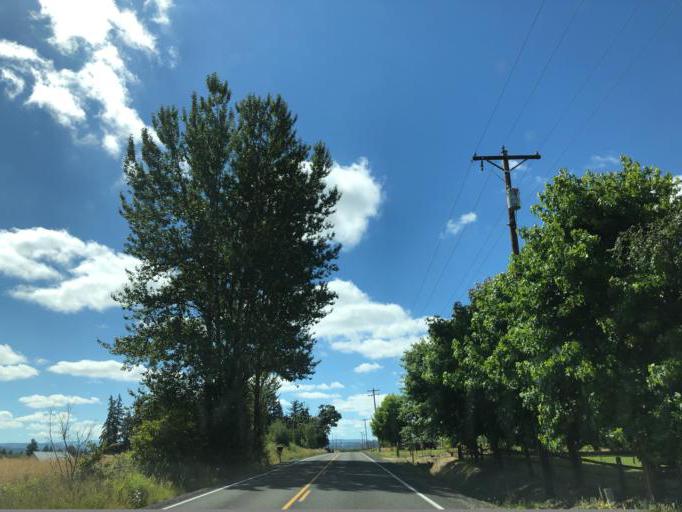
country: US
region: Oregon
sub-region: Marion County
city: Mount Angel
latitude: 45.0972
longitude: -122.7462
